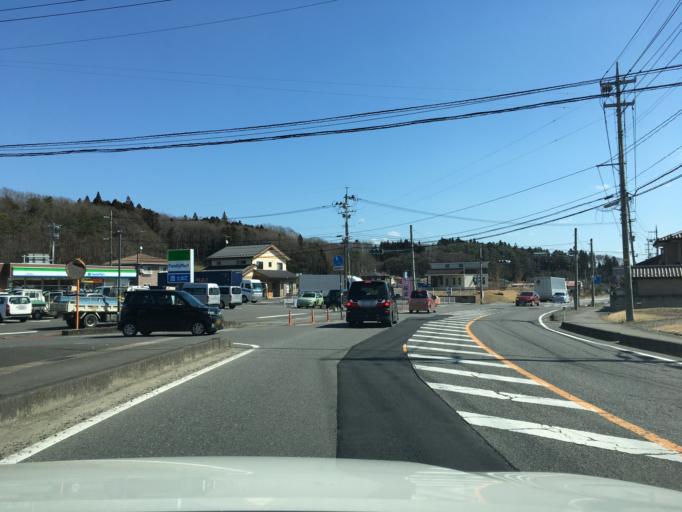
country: JP
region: Tochigi
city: Kuroiso
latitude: 37.1065
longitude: 140.1661
